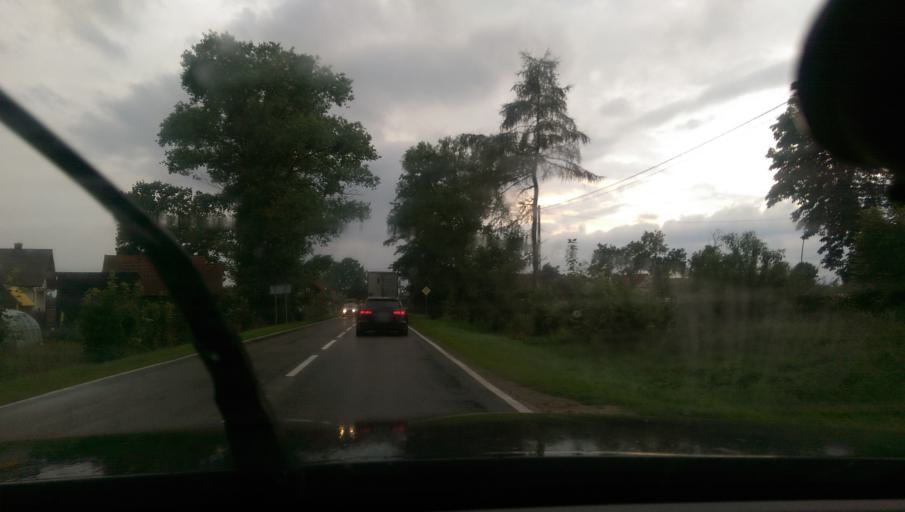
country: PL
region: Warmian-Masurian Voivodeship
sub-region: Powiat szczycienski
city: Swietajno
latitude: 53.5574
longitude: 21.1185
